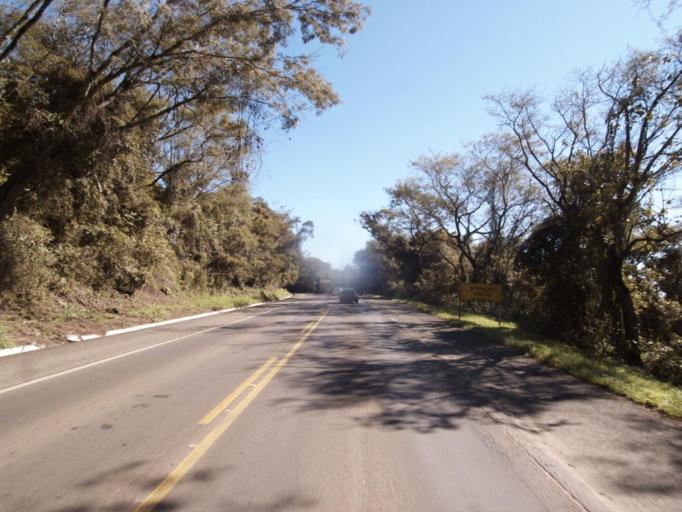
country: BR
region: Rio Grande do Sul
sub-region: Frederico Westphalen
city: Frederico Westphalen
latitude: -26.7983
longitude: -53.3403
